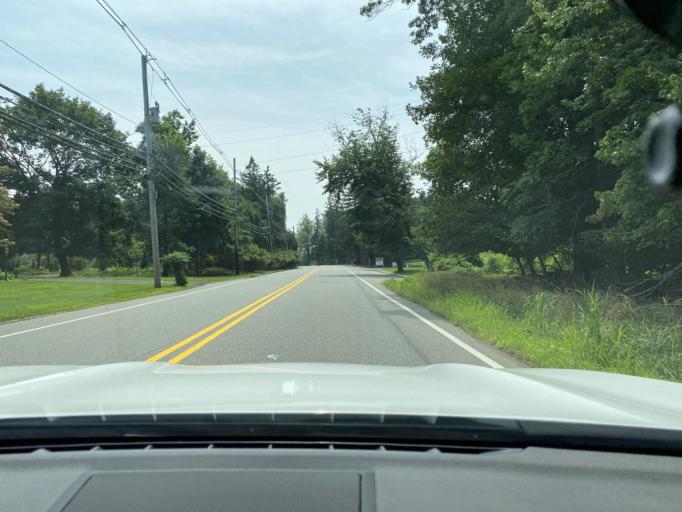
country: US
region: New Jersey
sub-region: Bergen County
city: Upper Saddle River
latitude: 41.0701
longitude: -74.1200
